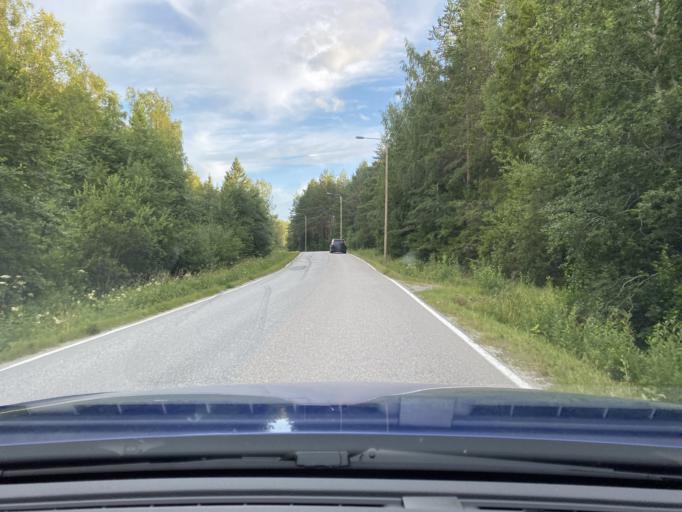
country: FI
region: Ostrobothnia
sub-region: Vaasa
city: Korsnaes
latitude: 62.9534
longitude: 21.1769
